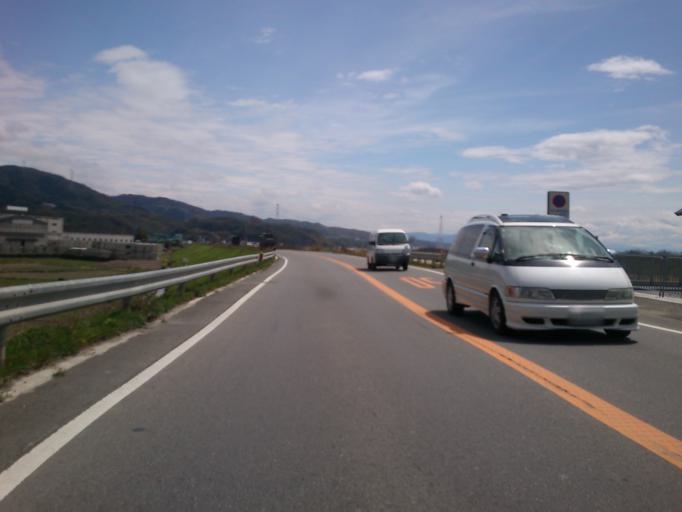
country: JP
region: Kyoto
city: Tanabe
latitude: 34.8199
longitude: 135.7963
